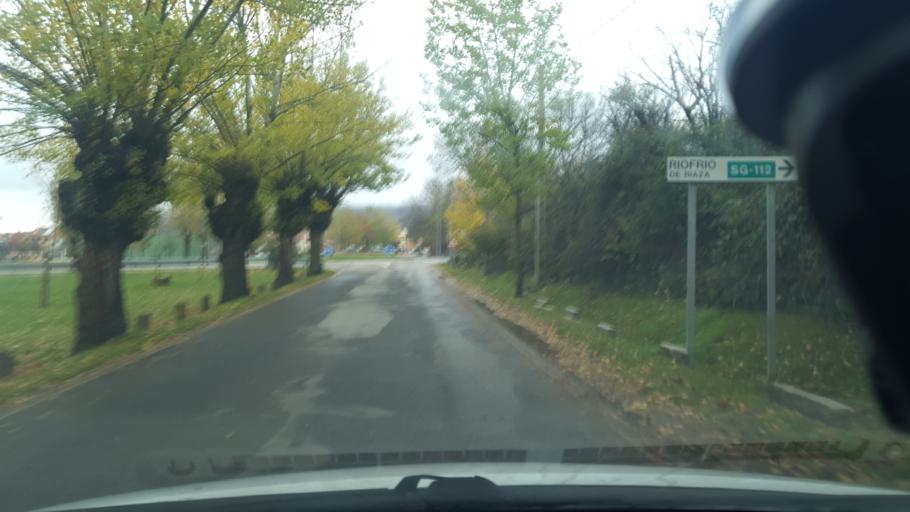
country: ES
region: Castille and Leon
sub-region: Provincia de Segovia
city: Riaza
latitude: 41.2766
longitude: -3.4832
